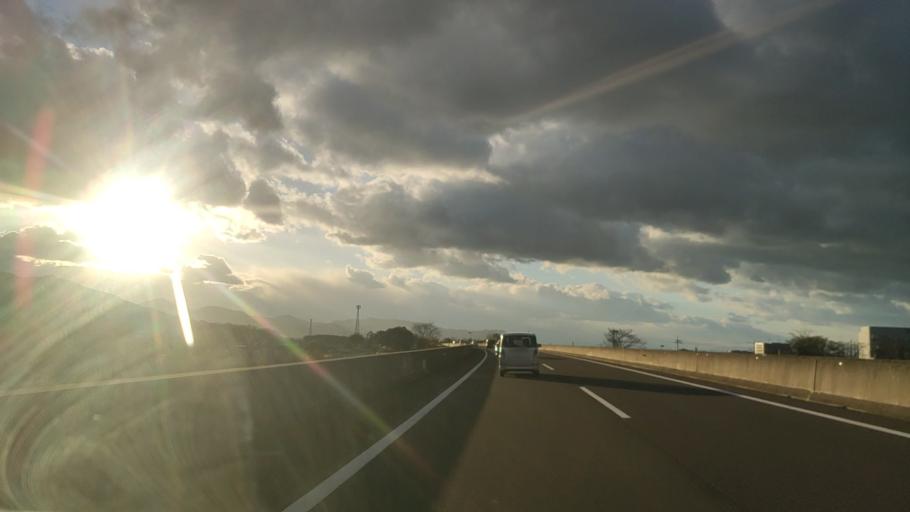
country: JP
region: Ehime
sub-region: Shikoku-chuo Shi
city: Matsuyama
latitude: 33.7885
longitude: 132.8833
